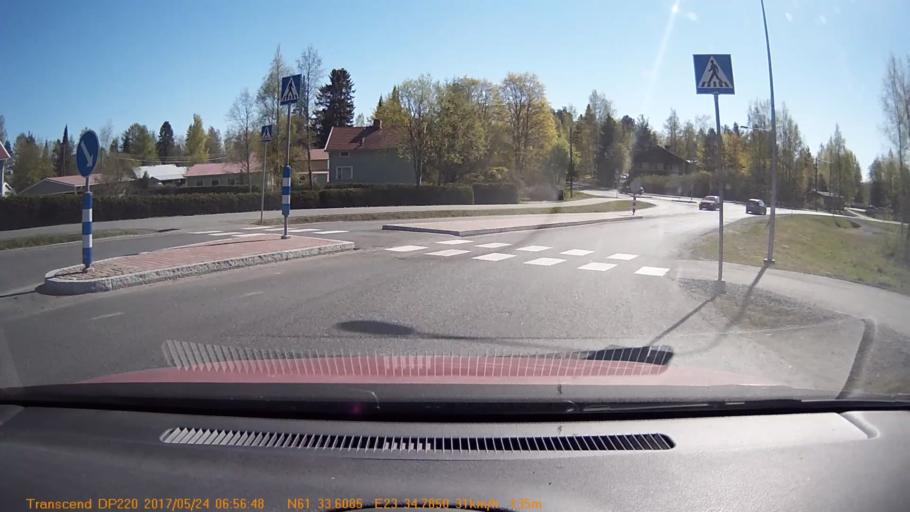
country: FI
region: Pirkanmaa
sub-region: Tampere
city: Yloejaervi
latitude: 61.5601
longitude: 23.5795
